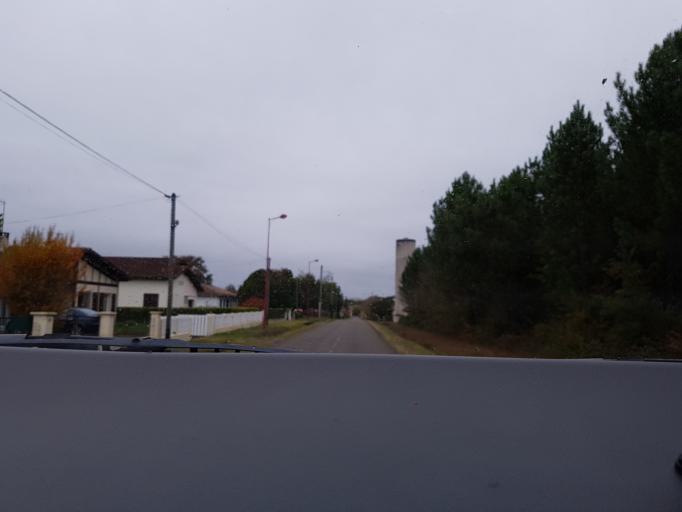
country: FR
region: Aquitaine
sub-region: Departement des Landes
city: Roquefort
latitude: 44.0955
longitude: -0.4001
